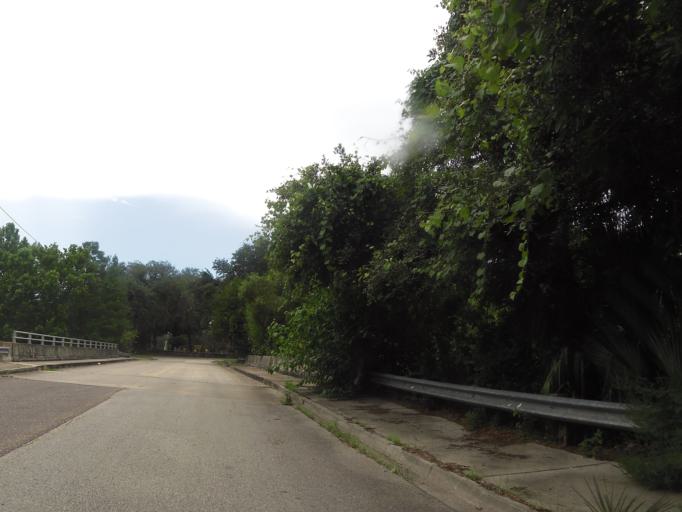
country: US
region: Florida
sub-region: Duval County
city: Jacksonville
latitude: 30.3637
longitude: -81.6493
